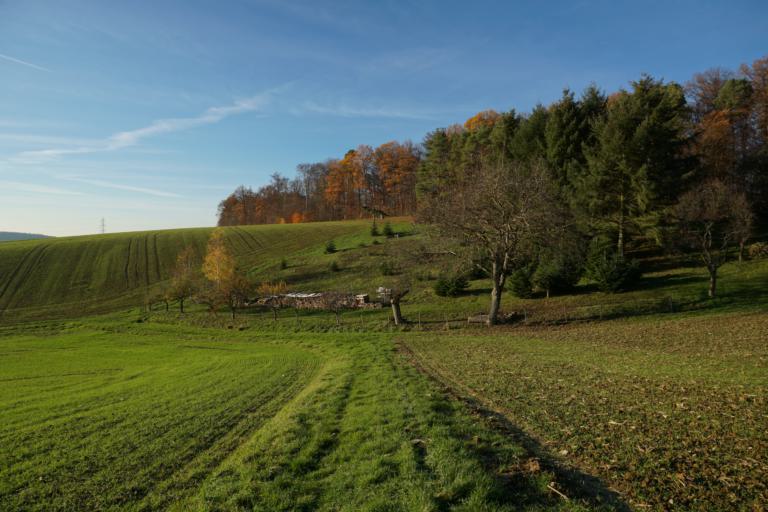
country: DE
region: Baden-Wuerttemberg
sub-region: Karlsruhe Region
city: Binau
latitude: 49.3298
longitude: 9.0479
